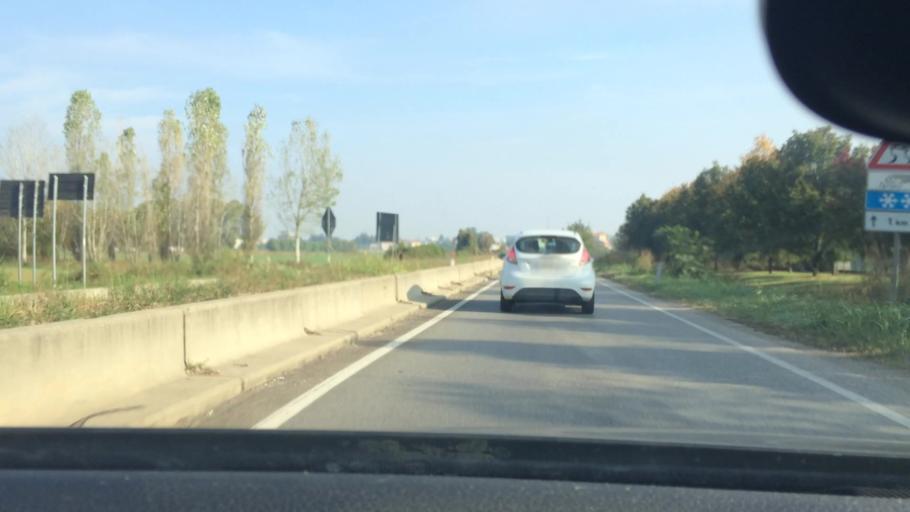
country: IT
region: Lombardy
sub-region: Citta metropolitana di Milano
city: San Giorgio Su Legnano
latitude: 45.5725
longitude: 8.9009
